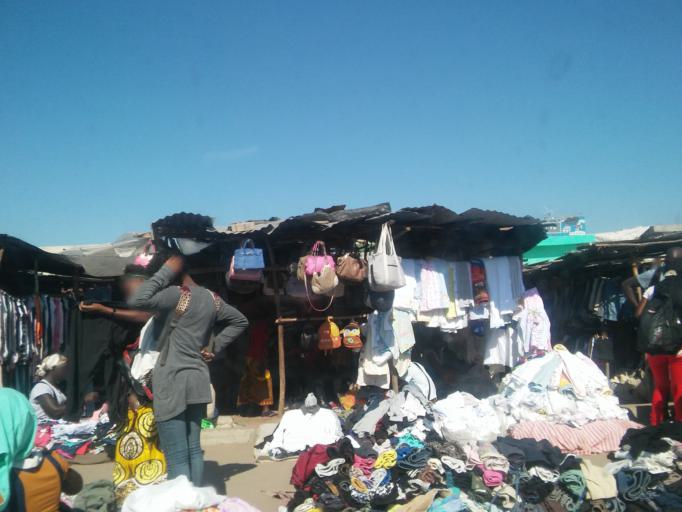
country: MZ
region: Maputo City
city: Maputo
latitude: -25.8309
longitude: 32.5738
